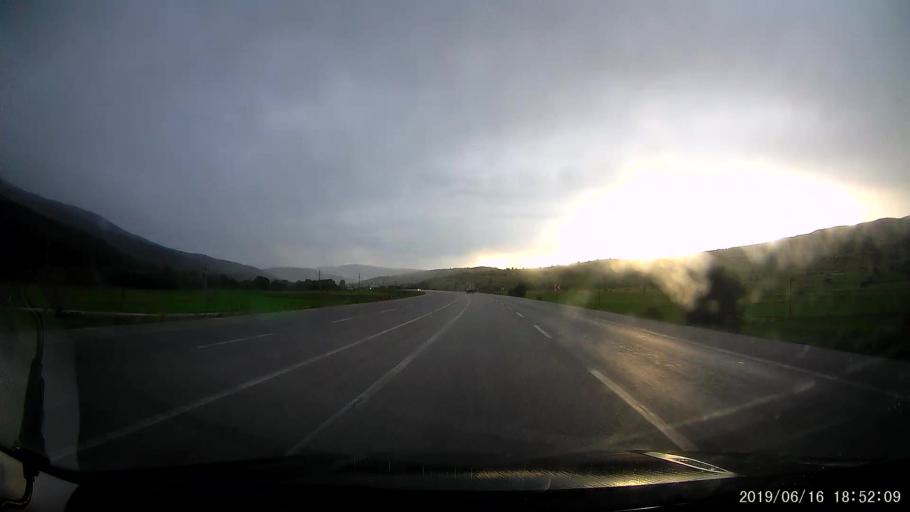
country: TR
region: Erzincan
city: Catalcam
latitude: 39.9031
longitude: 38.9092
